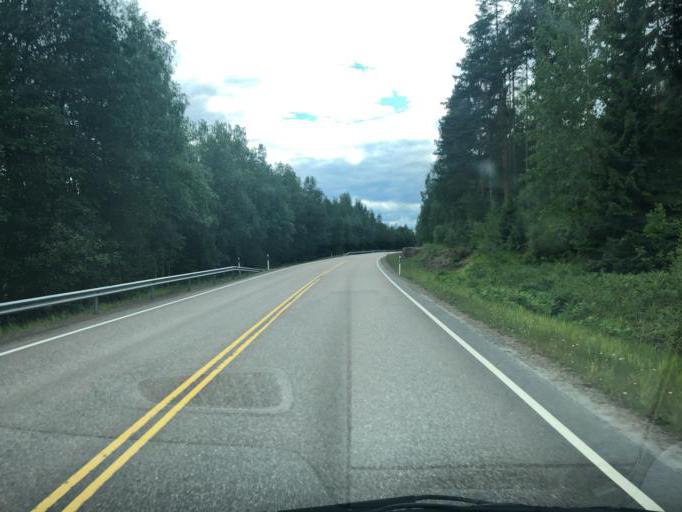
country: FI
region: Southern Savonia
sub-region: Mikkeli
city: Maentyharju
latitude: 61.1443
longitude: 27.1226
